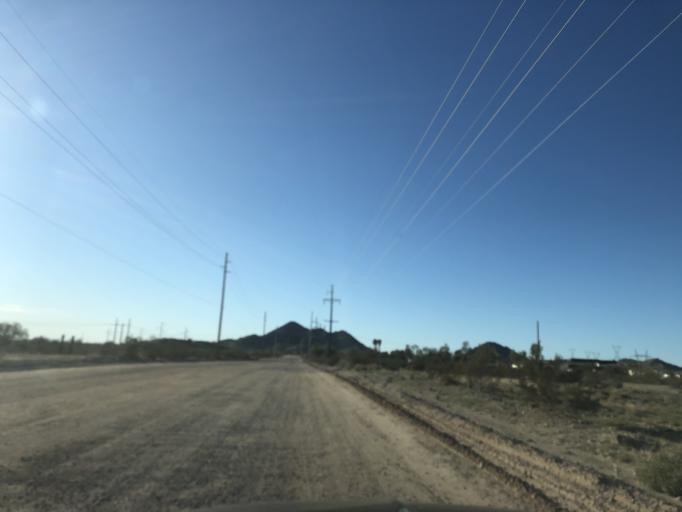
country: US
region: Arizona
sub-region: Maricopa County
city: Buckeye
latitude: 33.4354
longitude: -112.5929
